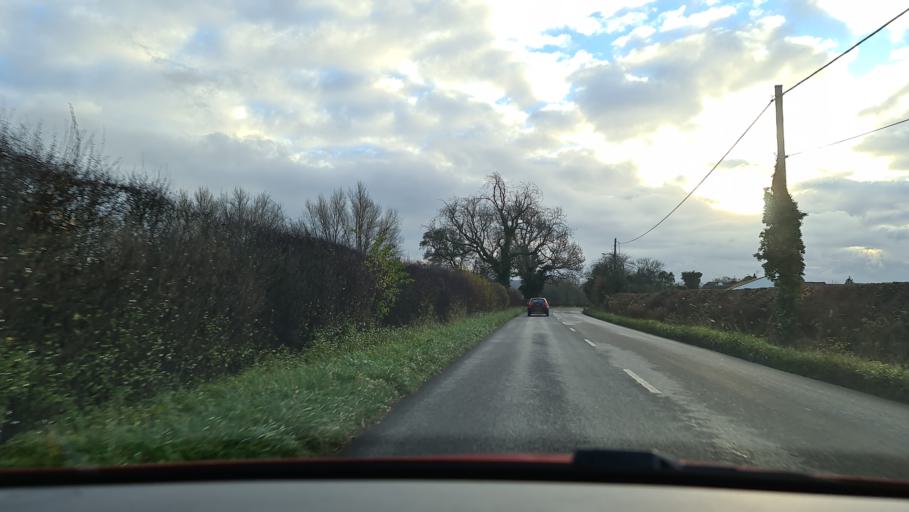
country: GB
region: England
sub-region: Buckinghamshire
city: Princes Risborough
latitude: 51.7290
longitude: -0.8551
